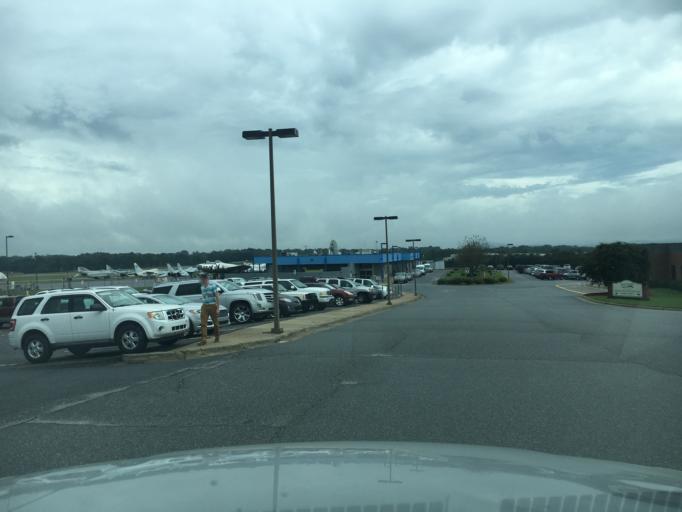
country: US
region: North Carolina
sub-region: Catawba County
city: Longview
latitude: 35.7431
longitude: -81.3883
